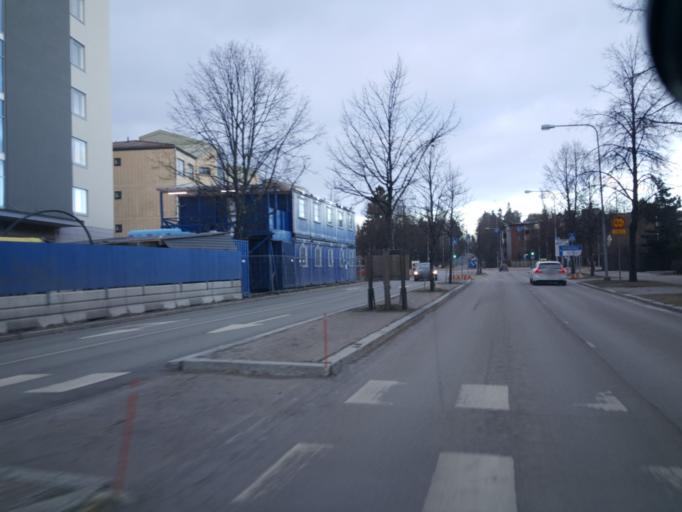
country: FI
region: Uusimaa
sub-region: Helsinki
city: Vantaa
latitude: 60.2958
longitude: 25.0338
